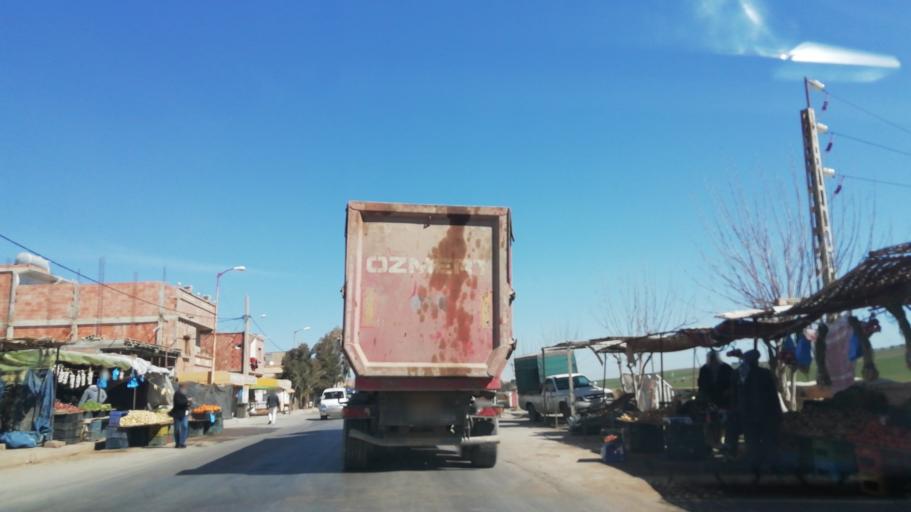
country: DZ
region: Oran
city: Es Senia
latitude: 35.5614
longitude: -0.5653
